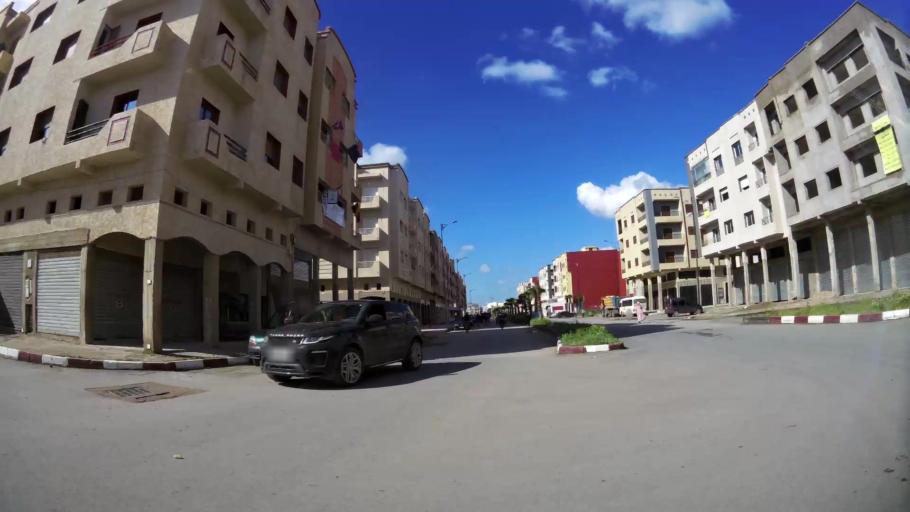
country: MA
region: Grand Casablanca
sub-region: Mediouna
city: Mediouna
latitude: 33.3868
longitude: -7.5325
